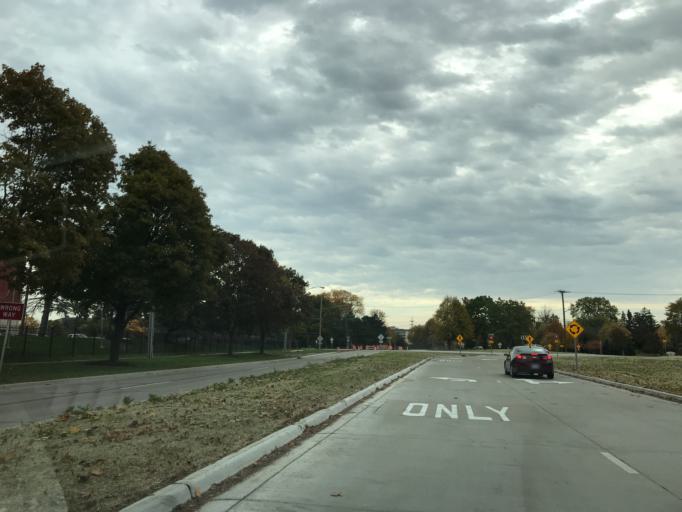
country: US
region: Michigan
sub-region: Oakland County
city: Bingham Farms
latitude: 42.4873
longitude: -83.2920
